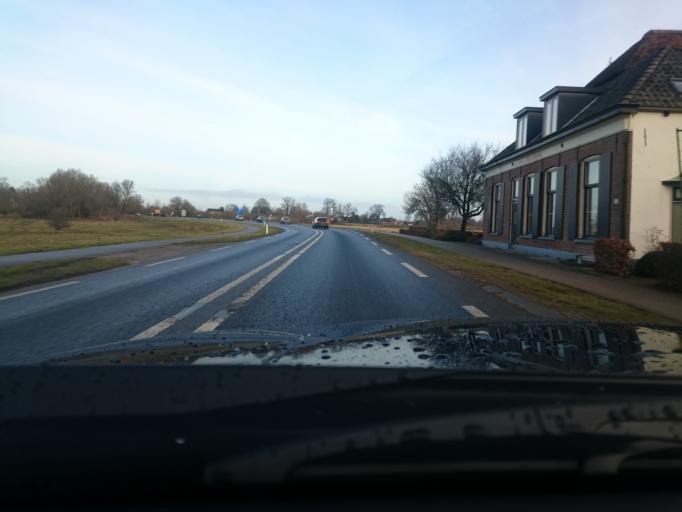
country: NL
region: Gelderland
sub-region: Gemeente Voorst
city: Voorst
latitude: 52.1530
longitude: 6.1457
